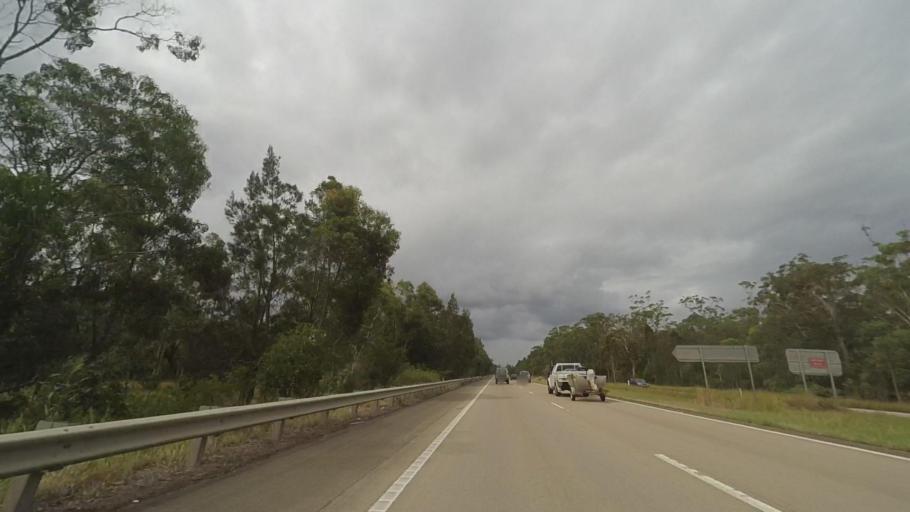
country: AU
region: New South Wales
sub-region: Port Stephens Shire
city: Raymond Terrace
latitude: -32.7251
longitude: 151.7863
